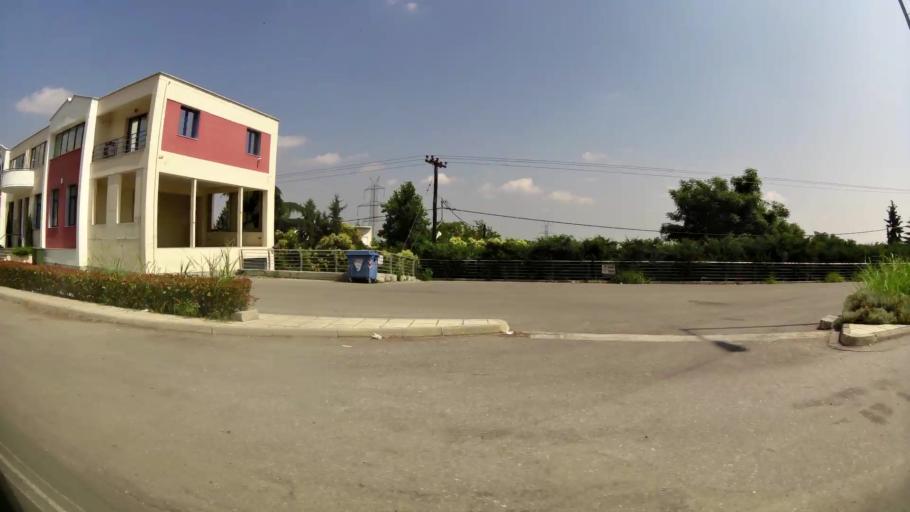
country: GR
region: Central Macedonia
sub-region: Nomos Imathias
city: Veroia
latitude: 40.5088
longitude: 22.2215
